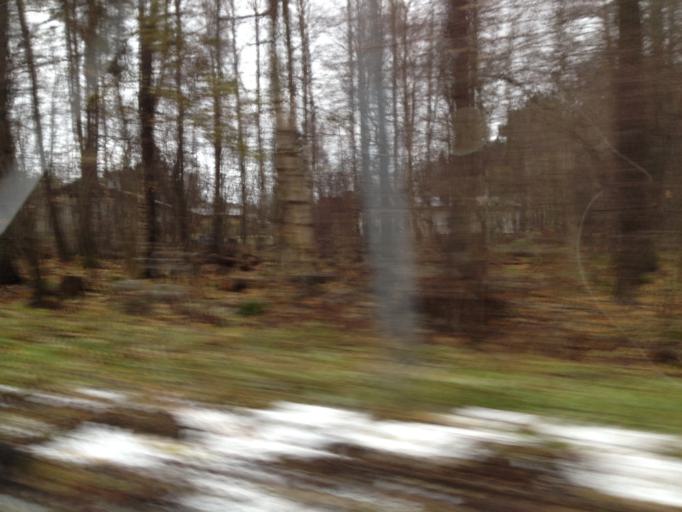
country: FI
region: Uusimaa
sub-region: Raaseporin
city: Hanko
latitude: 59.8330
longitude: 22.9354
